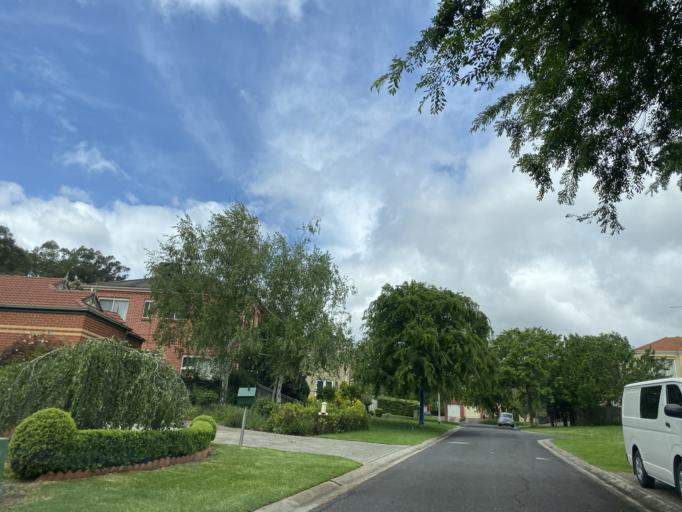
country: AU
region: Victoria
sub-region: Nillumbik
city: Eltham
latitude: -37.7595
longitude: 145.1440
